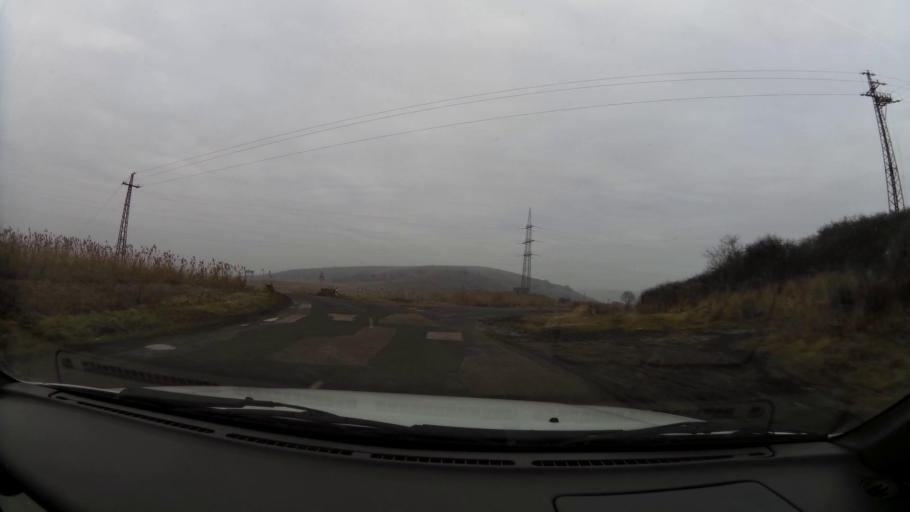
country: HU
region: Borsod-Abauj-Zemplen
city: Izsofalva
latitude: 48.2913
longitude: 20.6614
